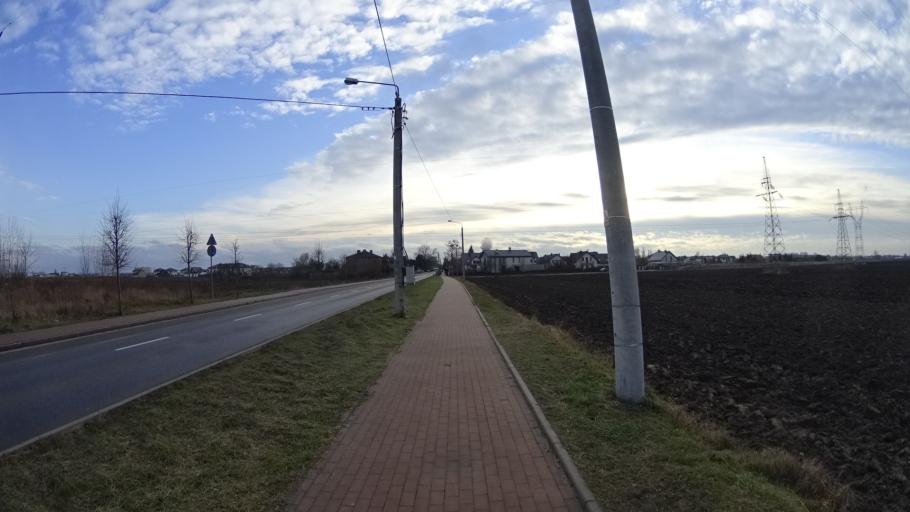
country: PL
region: Masovian Voivodeship
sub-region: Powiat warszawski zachodni
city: Ozarow Mazowiecki
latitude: 52.2280
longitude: 20.8023
